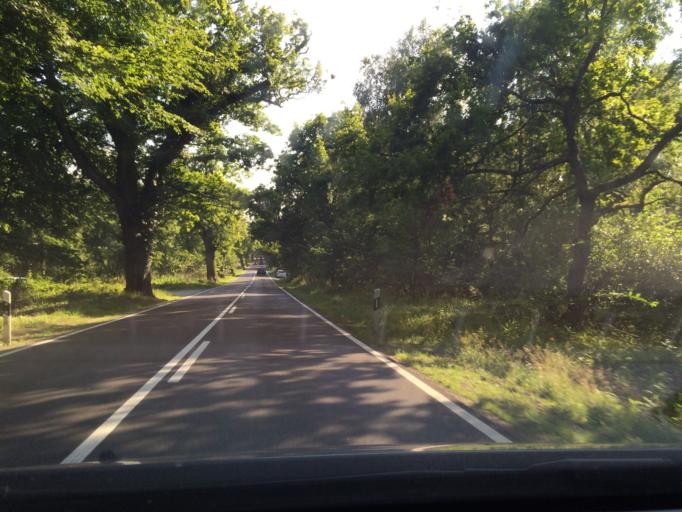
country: DE
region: Mecklenburg-Vorpommern
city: Ostseebad Binz
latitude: 54.4296
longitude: 13.5511
